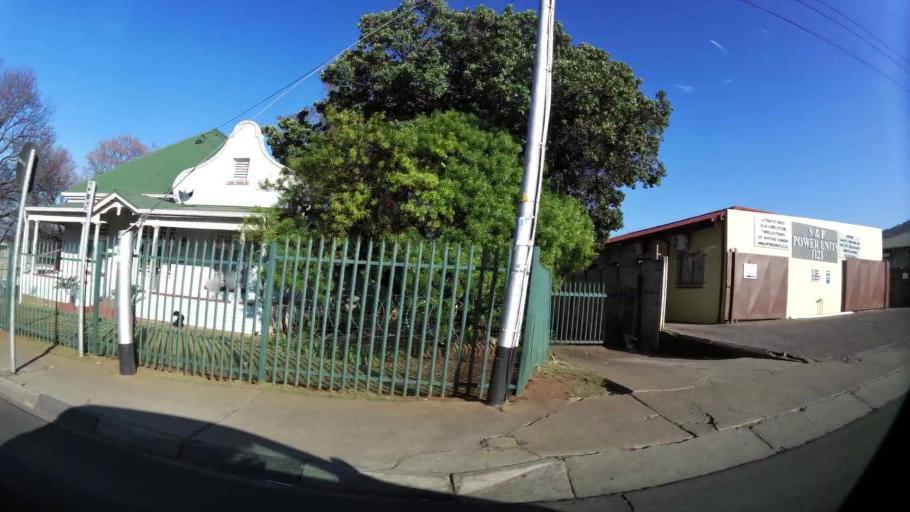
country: ZA
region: Gauteng
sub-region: City of Tshwane Metropolitan Municipality
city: Pretoria
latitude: -25.7003
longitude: 28.1995
